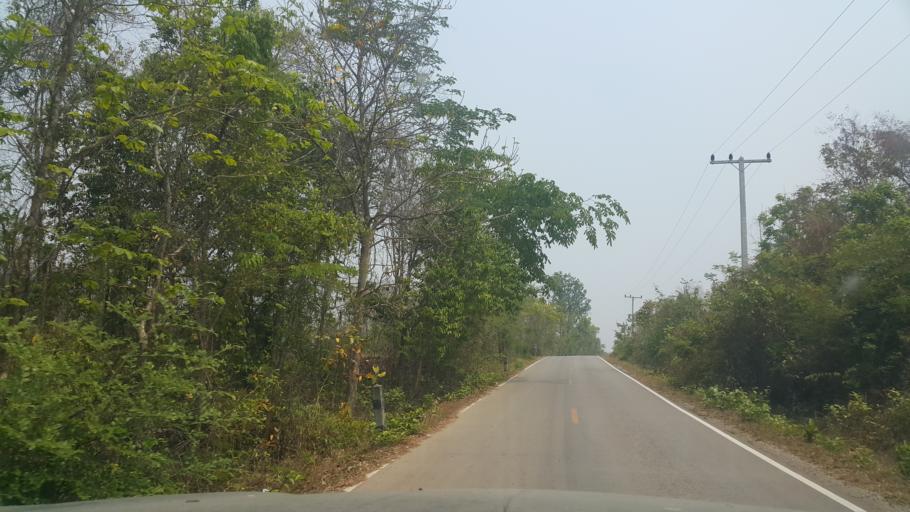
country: TH
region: Lampang
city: Sop Prap
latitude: 17.8954
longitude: 99.3148
